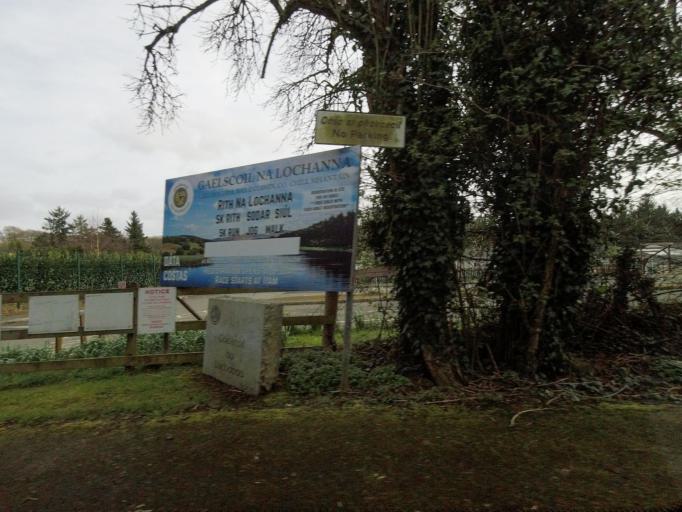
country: IE
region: Leinster
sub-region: Wicklow
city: Blessington
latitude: 53.1620
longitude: -6.5526
